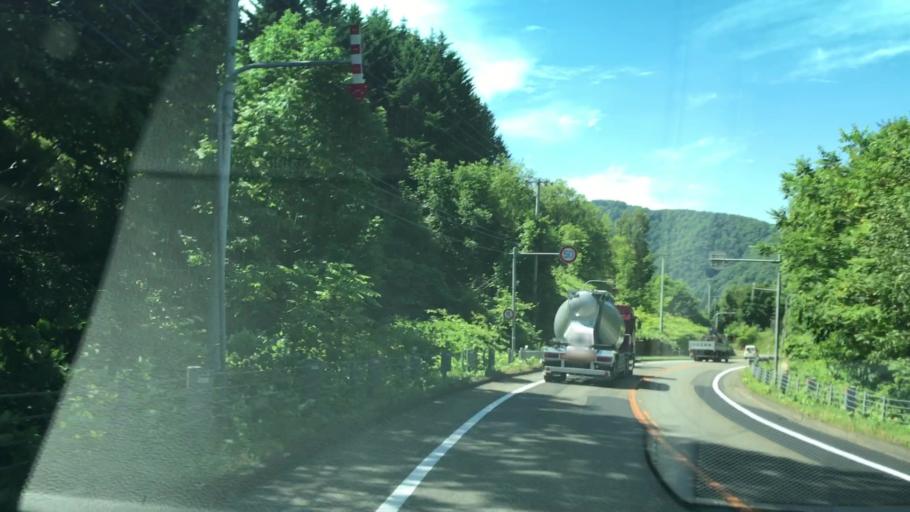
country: JP
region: Hokkaido
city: Shimo-furano
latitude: 42.9008
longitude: 142.4382
